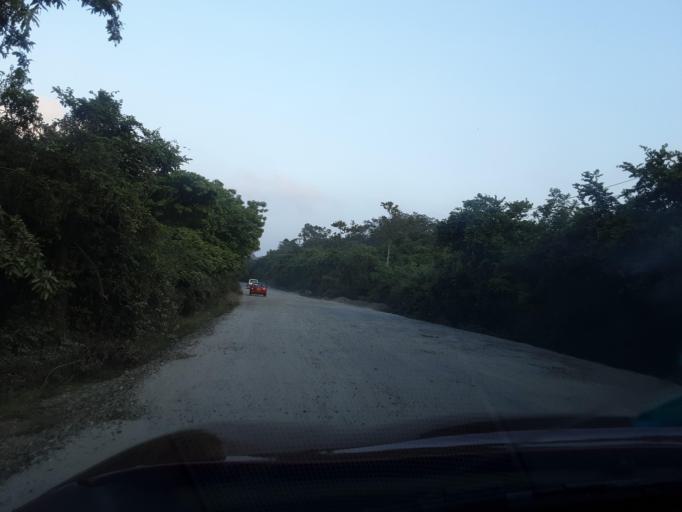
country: LK
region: Central
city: Dambulla
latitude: 7.8101
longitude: 80.7703
